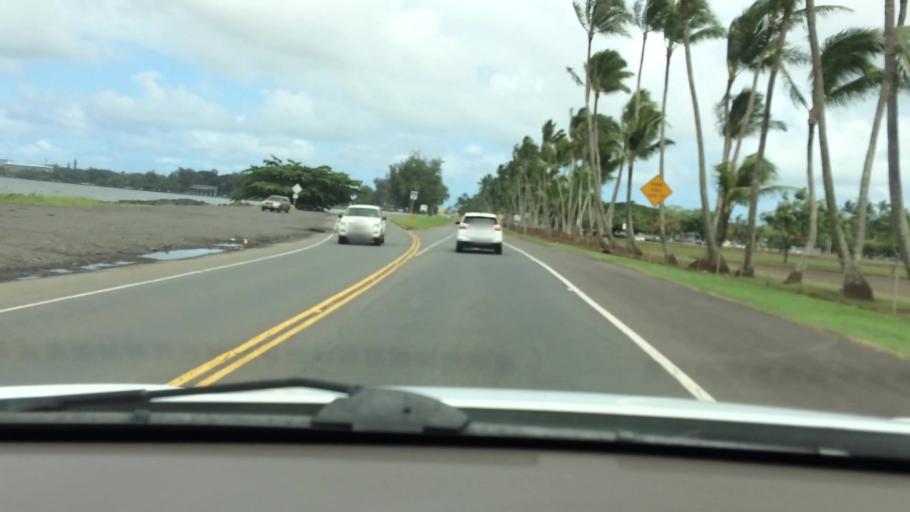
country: US
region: Hawaii
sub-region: Hawaii County
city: Hilo
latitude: 19.7235
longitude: -155.0820
